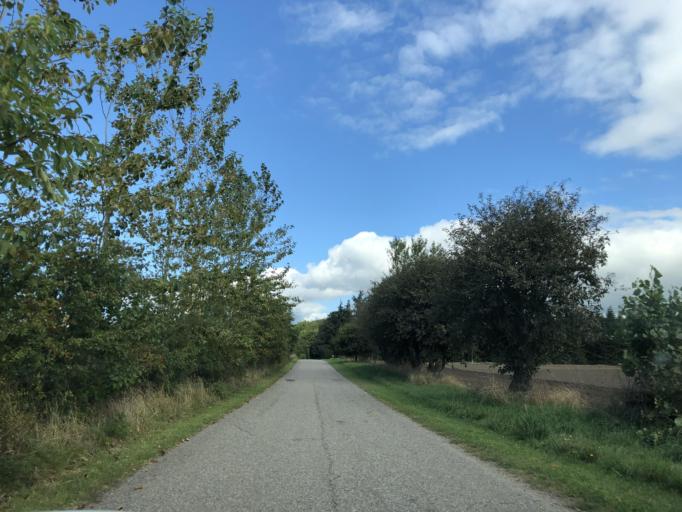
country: DK
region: Central Jutland
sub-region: Viborg Kommune
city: Viborg
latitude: 56.5578
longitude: 9.3097
